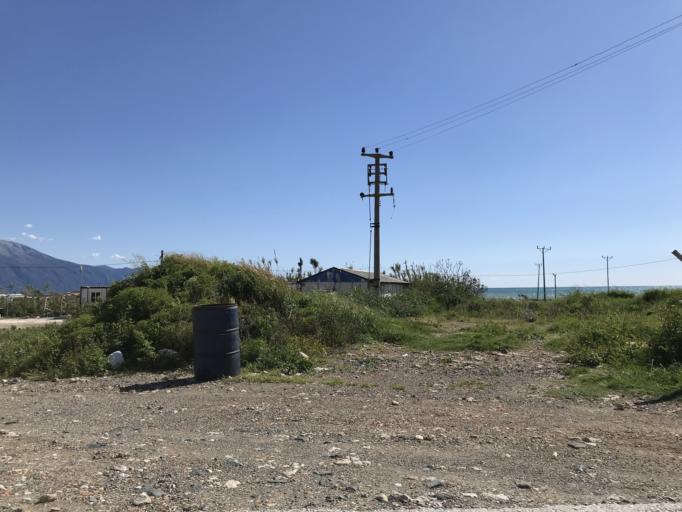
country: TR
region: Hatay
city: Samandag
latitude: 36.1140
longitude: 35.9286
